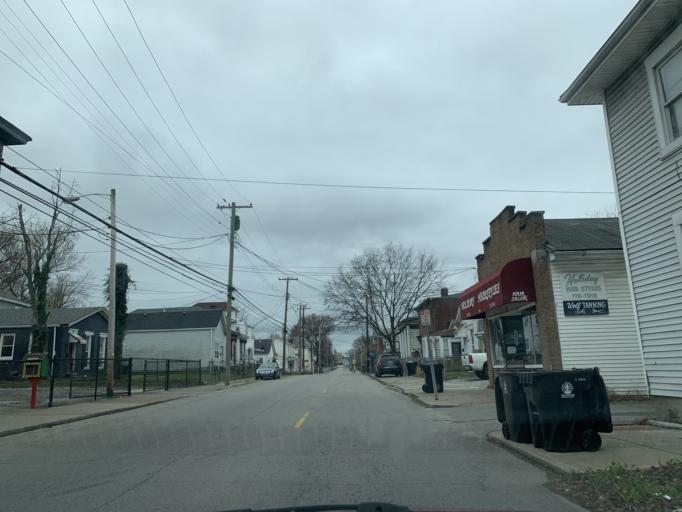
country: US
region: Kentucky
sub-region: Jefferson County
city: Louisville
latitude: 38.2708
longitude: -85.7902
